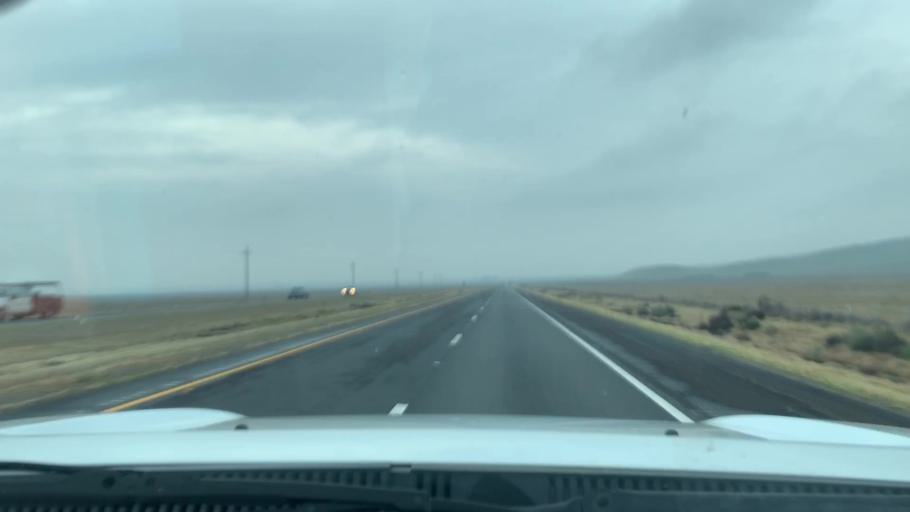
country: US
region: California
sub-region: San Luis Obispo County
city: Shandon
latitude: 35.6571
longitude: -120.0532
